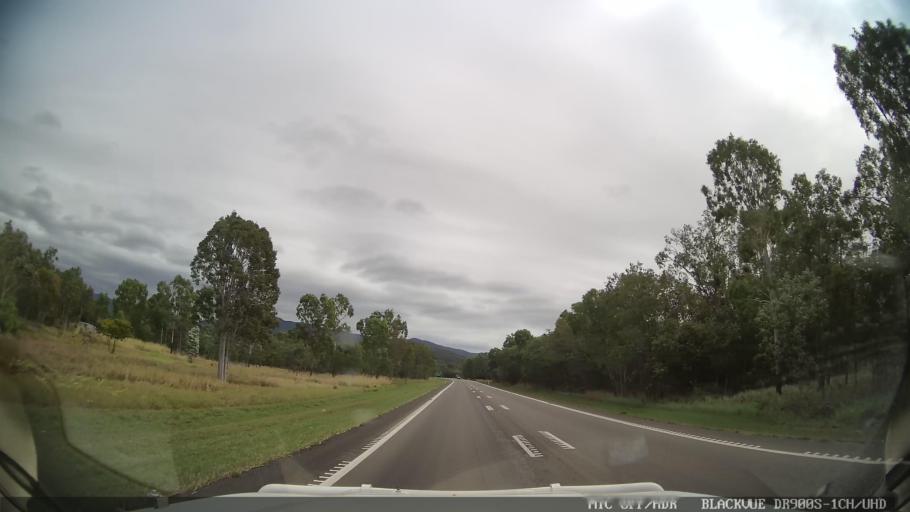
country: AU
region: Queensland
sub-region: Hinchinbrook
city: Ingham
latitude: -18.9545
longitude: 146.2947
